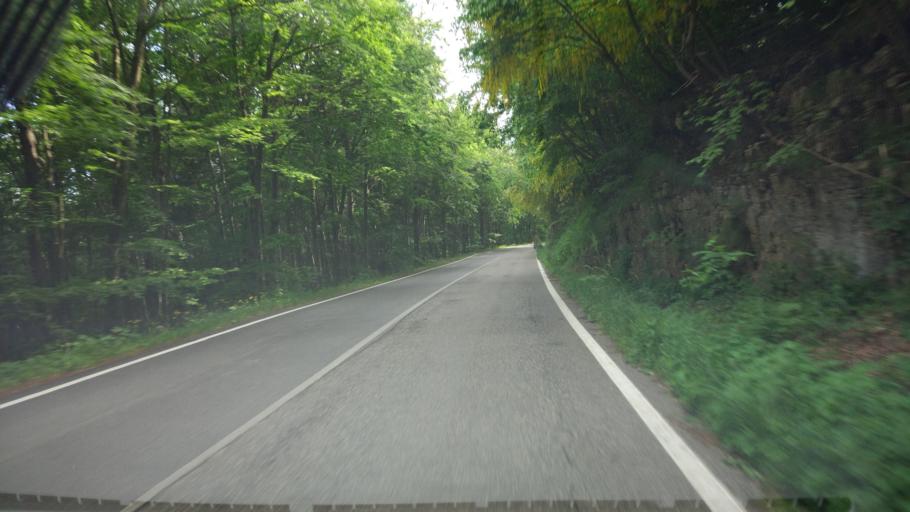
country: IT
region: Veneto
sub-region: Provincia di Verona
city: Bosco Chiesanuova
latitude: 45.6364
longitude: 11.0425
